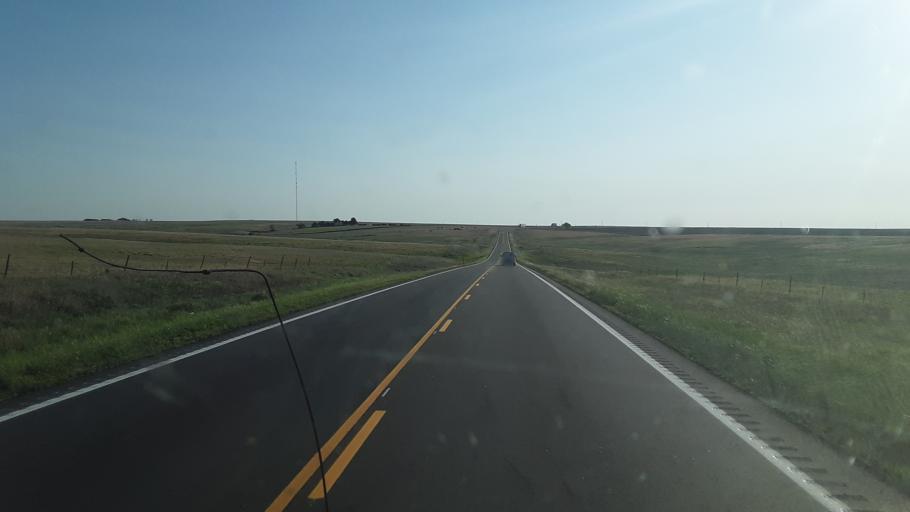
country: US
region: Kansas
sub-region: Hodgeman County
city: Jetmore
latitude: 38.0811
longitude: -99.9814
